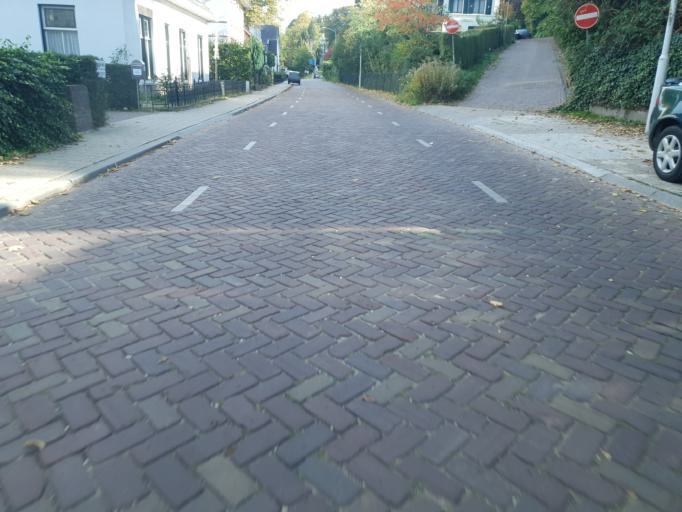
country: NL
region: Gelderland
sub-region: Gemeente Groesbeek
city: Berg en Dal
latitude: 51.8308
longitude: 5.9195
